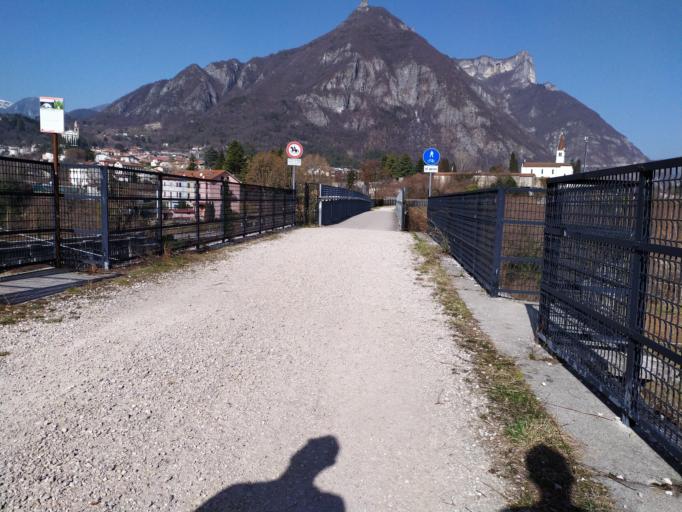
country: IT
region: Veneto
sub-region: Provincia di Vicenza
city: Arsiero
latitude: 45.7977
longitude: 11.3592
